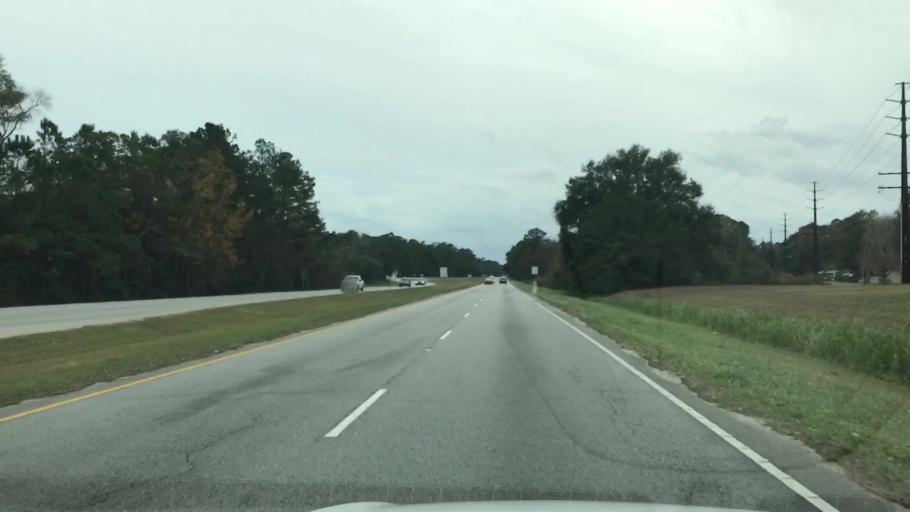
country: US
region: South Carolina
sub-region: Georgetown County
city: Murrells Inlet
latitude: 33.5319
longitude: -79.0606
